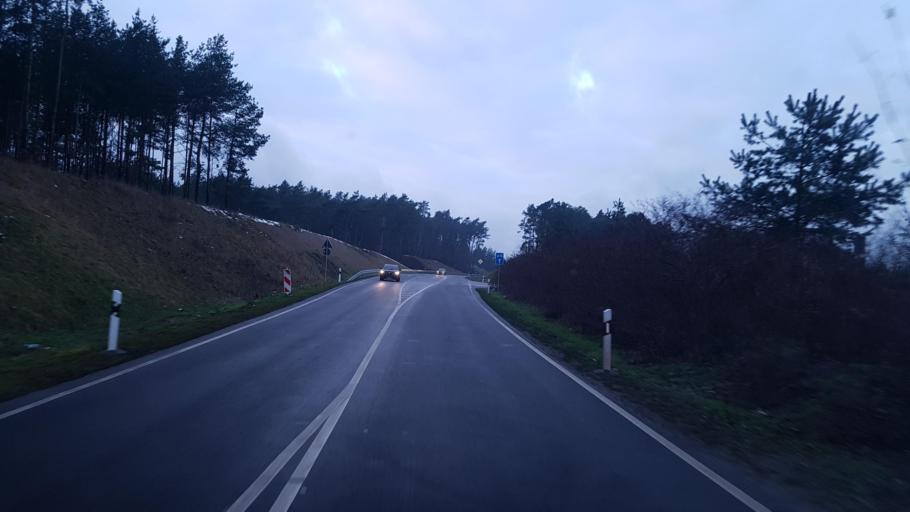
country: DE
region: Brandenburg
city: Wildau
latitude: 52.3149
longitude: 13.6618
